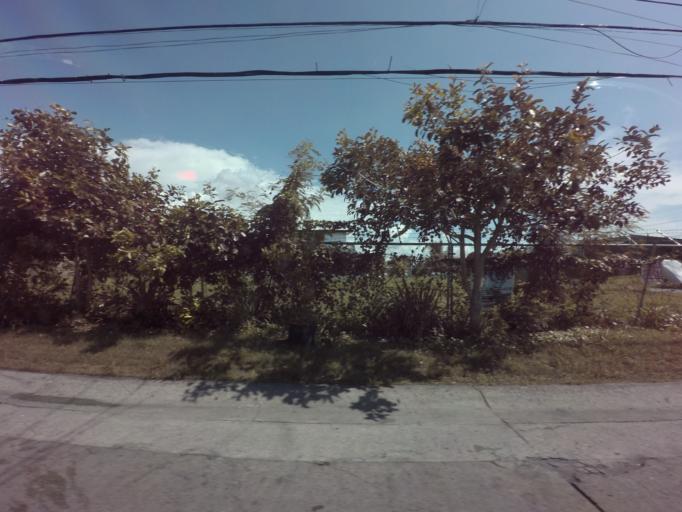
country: PH
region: Calabarzon
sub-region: Province of Rizal
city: Las Pinas
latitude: 14.4302
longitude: 120.9905
